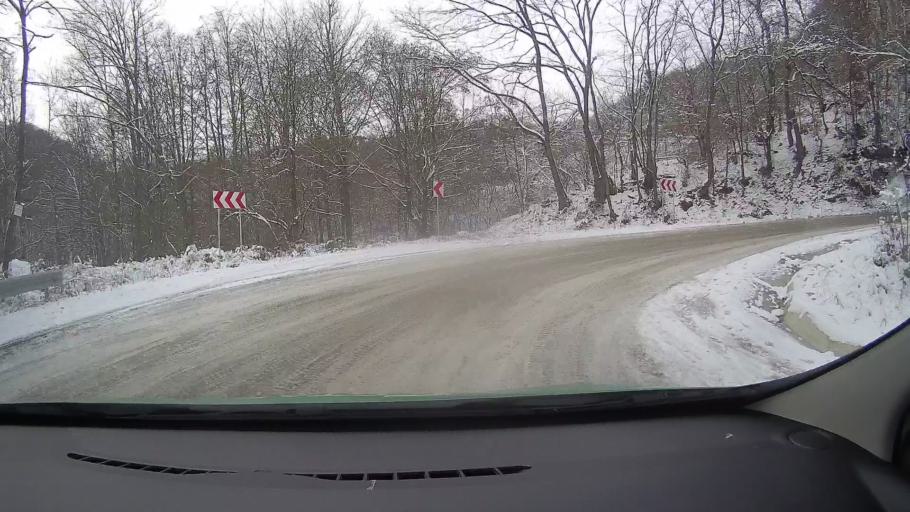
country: RO
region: Alba
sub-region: Comuna Almasu Mare
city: Almasu Mare
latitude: 46.0958
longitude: 23.1734
